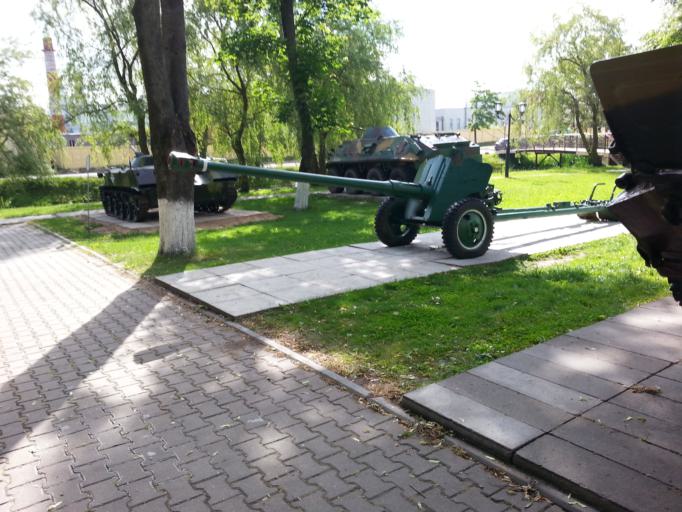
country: BY
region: Vitebsk
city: Hlybokaye
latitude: 55.1389
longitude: 27.6911
